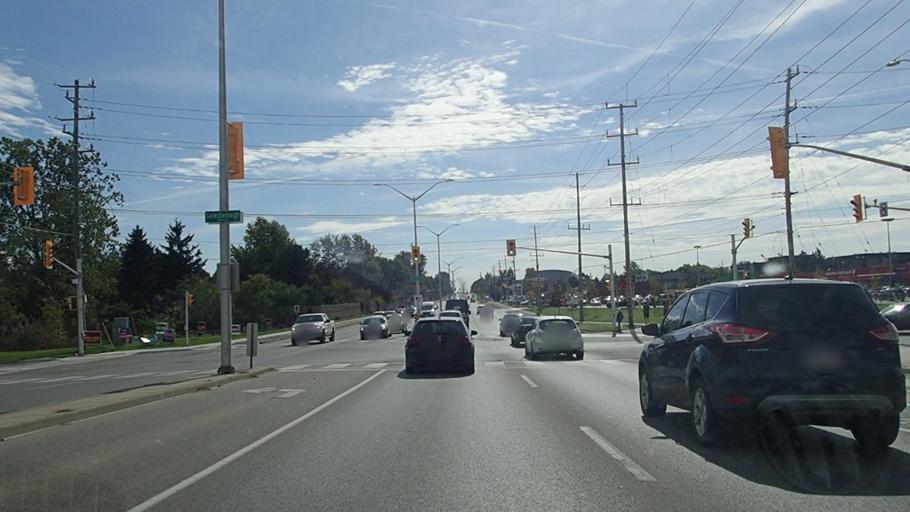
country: CA
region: Ontario
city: London
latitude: 43.0072
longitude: -81.3045
